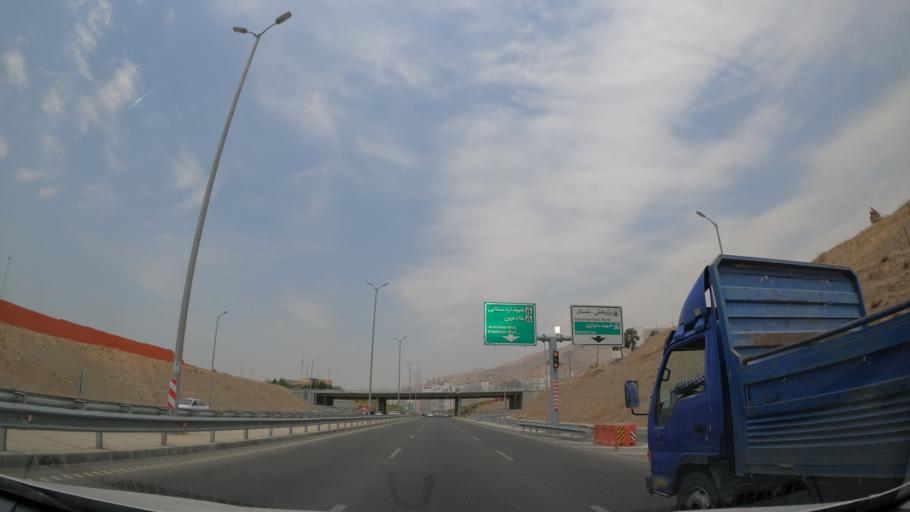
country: IR
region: Tehran
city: Shahr-e Qods
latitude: 35.7492
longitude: 51.1752
